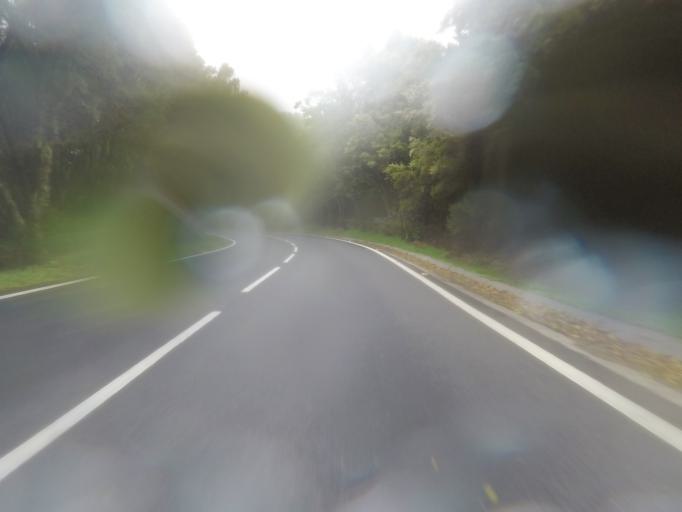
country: ES
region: Canary Islands
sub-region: Provincia de Santa Cruz de Tenerife
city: Vallehermosa
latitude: 28.1373
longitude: -17.2815
